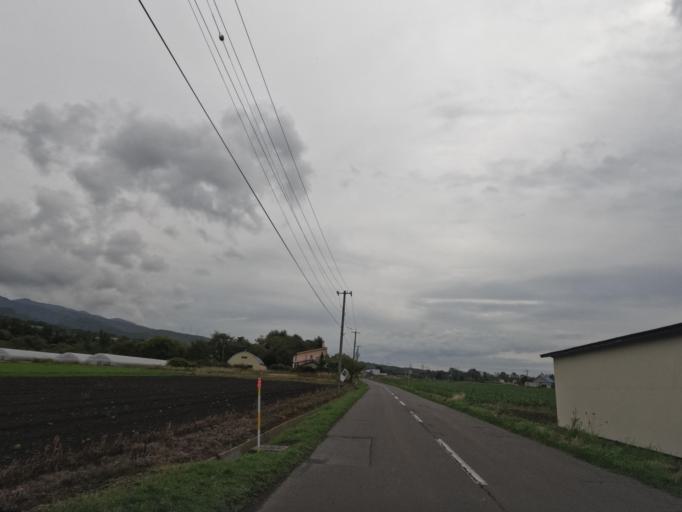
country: JP
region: Hokkaido
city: Date
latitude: 42.4389
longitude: 140.9038
